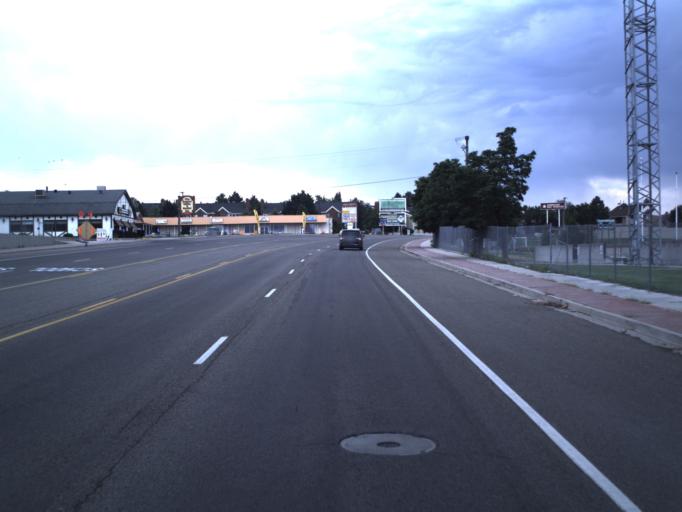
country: US
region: Utah
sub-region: Salt Lake County
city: Sandy City
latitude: 40.6189
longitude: -111.8662
